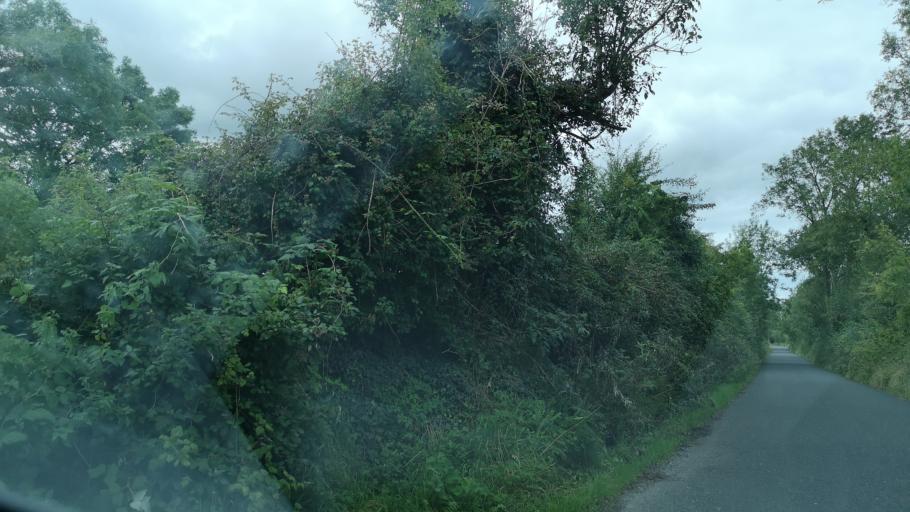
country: IE
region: Connaught
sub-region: County Galway
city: Loughrea
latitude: 53.1586
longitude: -8.4560
